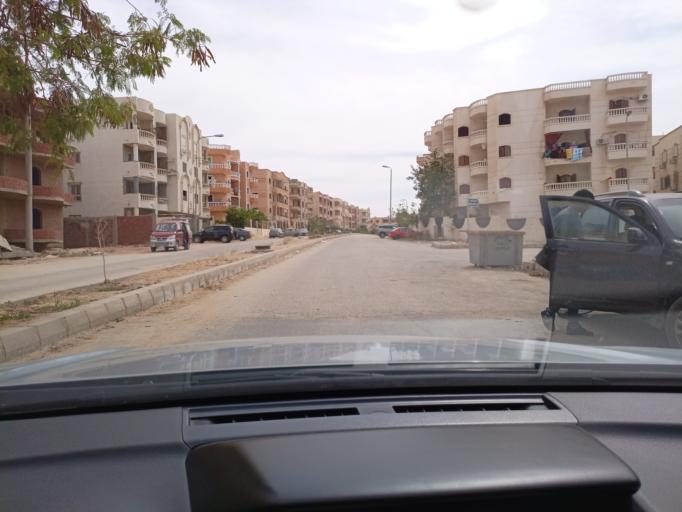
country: EG
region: Muhafazat al Qalyubiyah
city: Al Khankah
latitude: 30.2431
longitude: 31.4883
